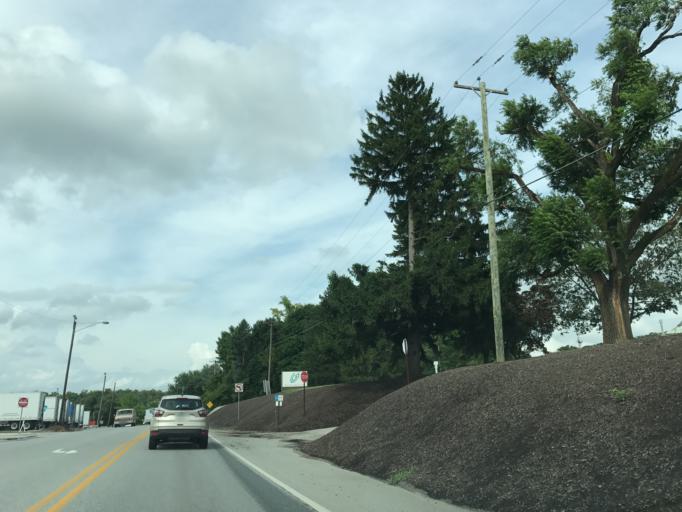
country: US
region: Pennsylvania
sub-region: York County
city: Spring Grove
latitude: 39.8668
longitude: -76.8655
